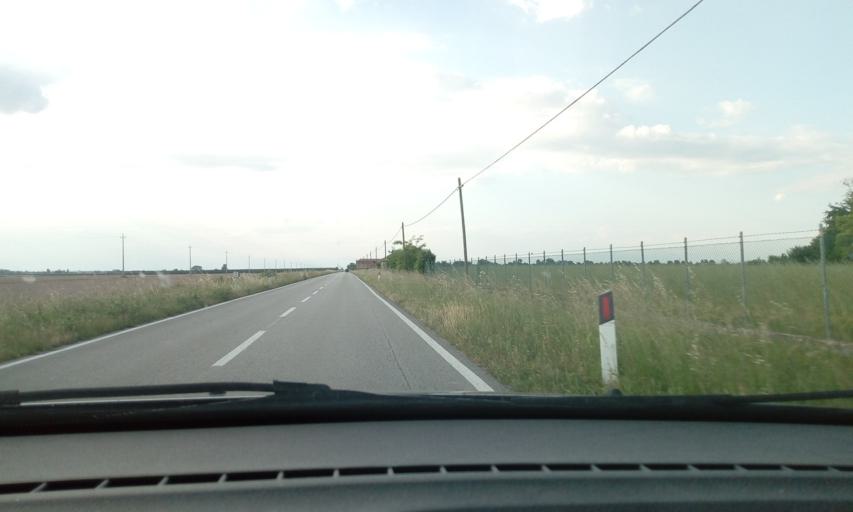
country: IT
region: Friuli Venezia Giulia
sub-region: Provincia di Udine
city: Pertegada
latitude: 45.7433
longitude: 13.0622
